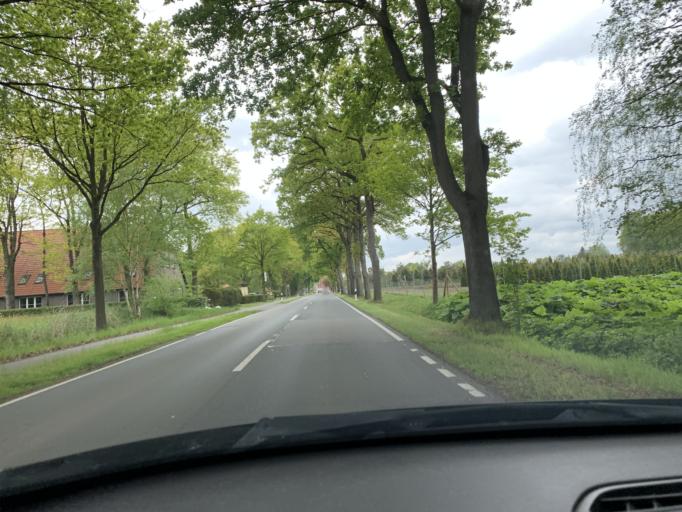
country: DE
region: Lower Saxony
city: Bad Zwischenahn
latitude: 53.2135
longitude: 8.0263
